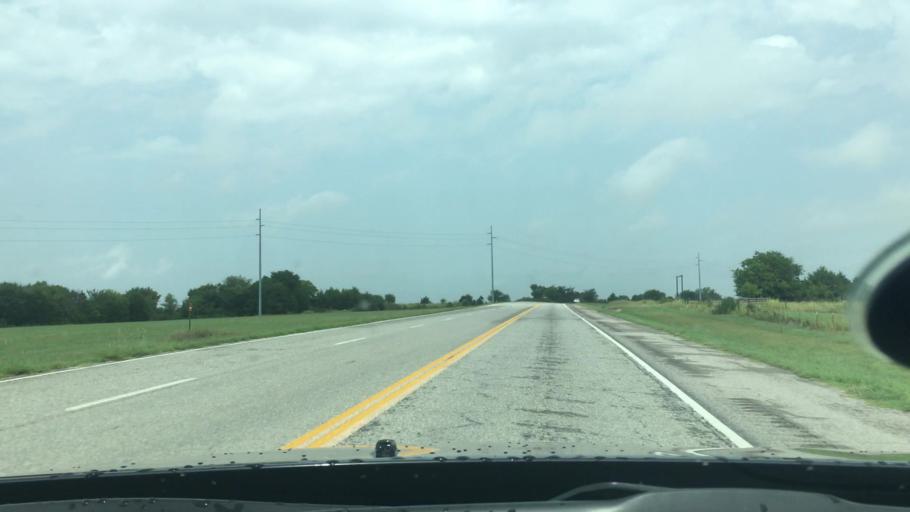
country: US
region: Oklahoma
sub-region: Johnston County
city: Tishomingo
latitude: 34.2800
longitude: -96.7798
